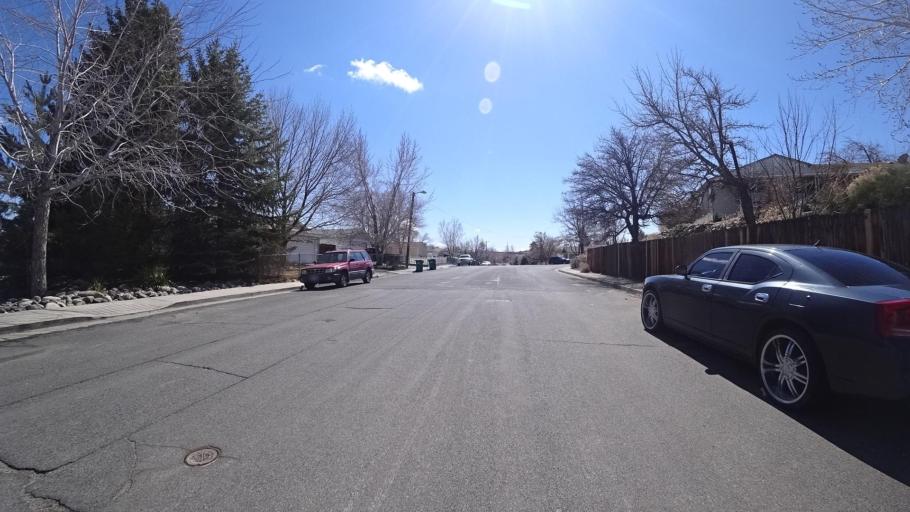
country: US
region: Nevada
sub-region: Washoe County
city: Golden Valley
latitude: 39.5923
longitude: -119.8432
